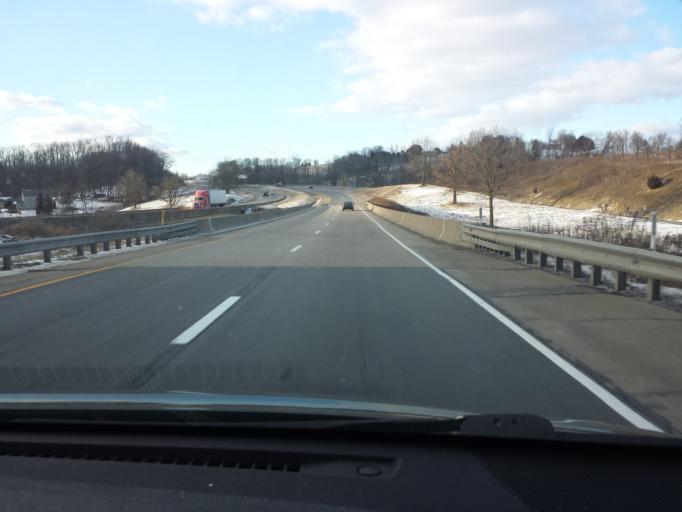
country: US
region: Pennsylvania
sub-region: Northumberland County
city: Milton
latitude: 41.0197
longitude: -76.7917
